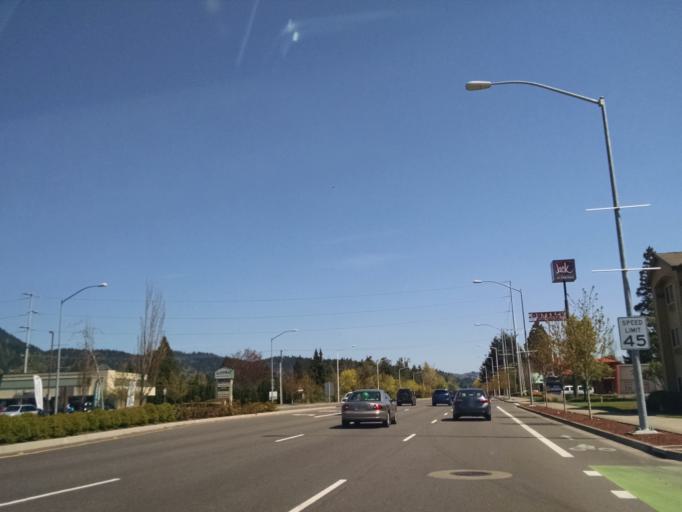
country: US
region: Oregon
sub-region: Lane County
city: Springfield
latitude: 44.0840
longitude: -123.0405
